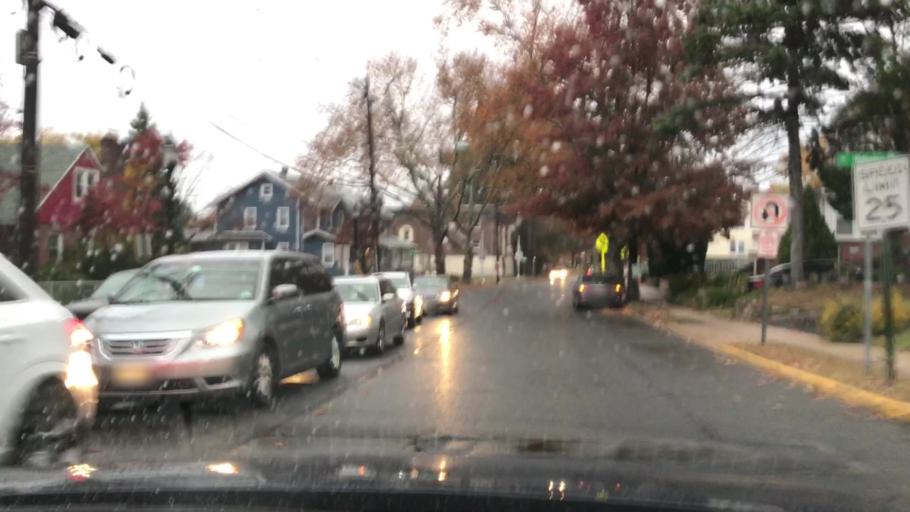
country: US
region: New Jersey
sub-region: Bergen County
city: Bogota
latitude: 40.8773
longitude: -74.0250
